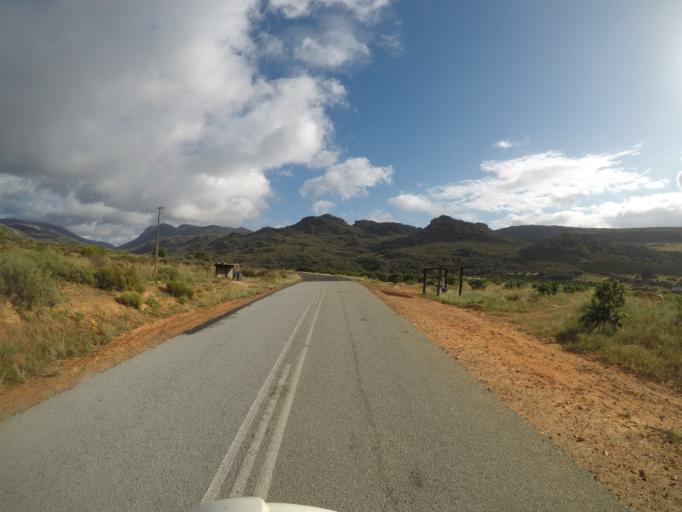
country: ZA
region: Western Cape
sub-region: West Coast District Municipality
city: Clanwilliam
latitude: -32.4244
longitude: 18.9346
